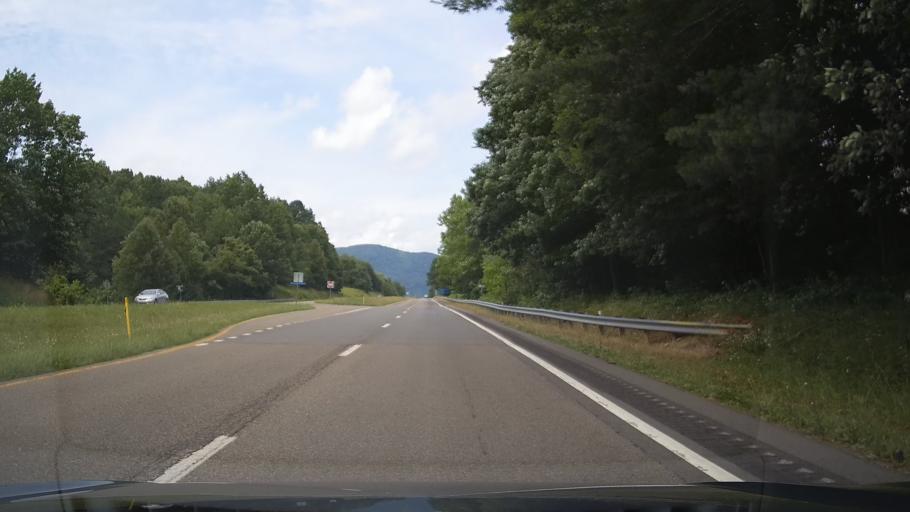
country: US
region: Virginia
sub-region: Wise County
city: Big Stone Gap
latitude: 36.8454
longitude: -82.7612
